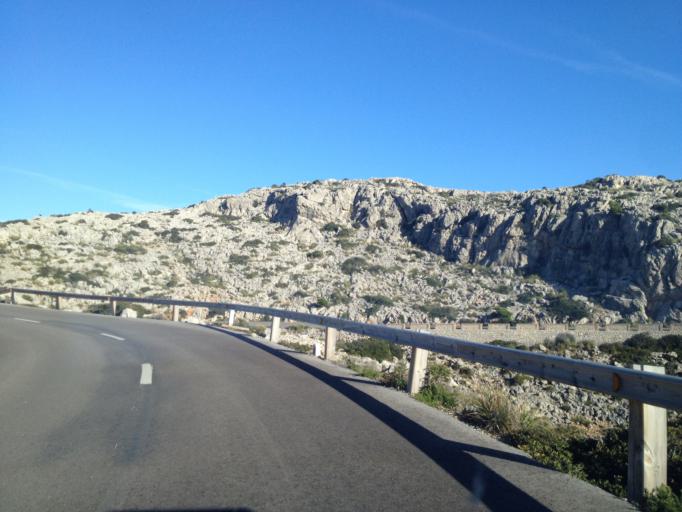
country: ES
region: Balearic Islands
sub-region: Illes Balears
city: Alcudia
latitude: 39.9568
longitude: 3.2084
